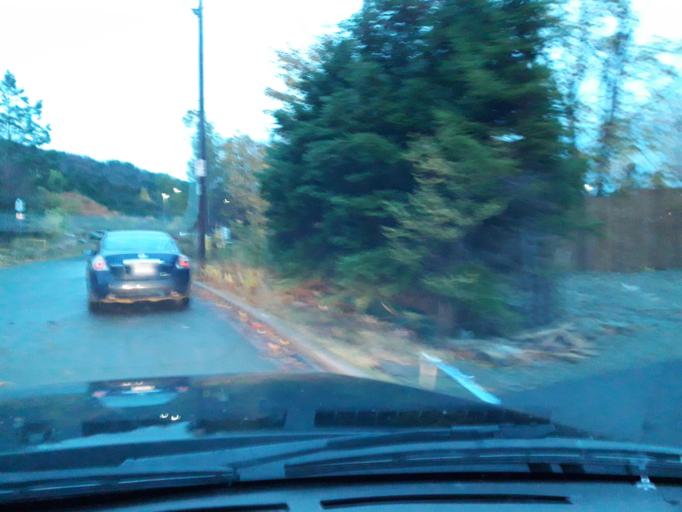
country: CA
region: Newfoundland and Labrador
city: St. John's
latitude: 47.5697
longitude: -52.7483
